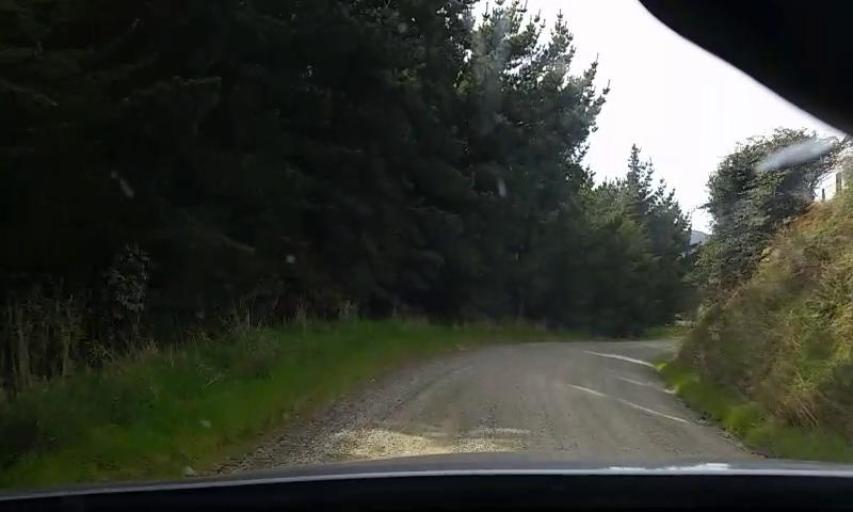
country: NZ
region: Otago
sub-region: Clutha District
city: Papatowai
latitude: -46.6276
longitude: 168.9905
